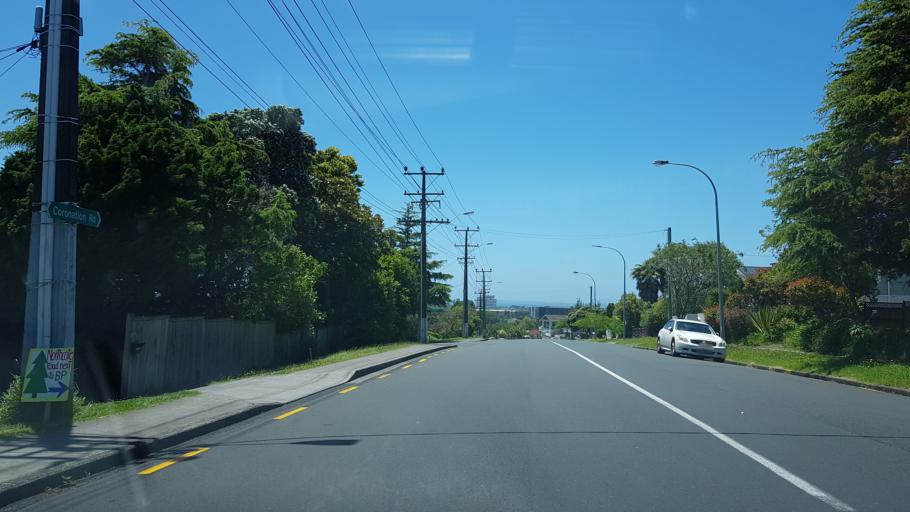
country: NZ
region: Auckland
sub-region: Auckland
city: North Shore
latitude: -36.7886
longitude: 174.7386
